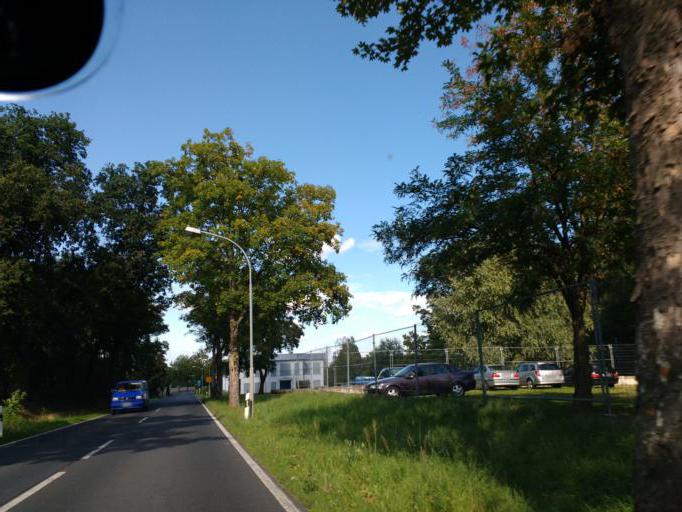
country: DE
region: Brandenburg
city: Mittenwalde
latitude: 52.2470
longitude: 13.5665
